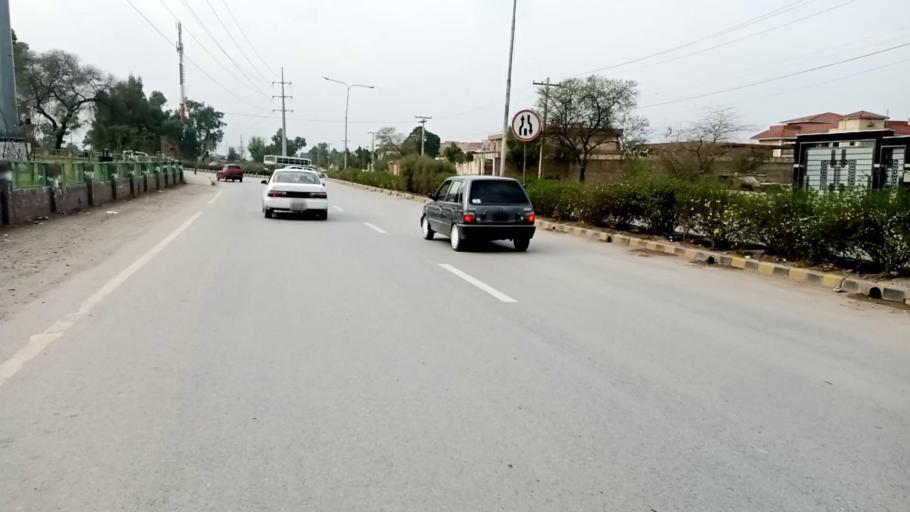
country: PK
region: Khyber Pakhtunkhwa
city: Peshawar
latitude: 33.9599
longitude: 71.4444
